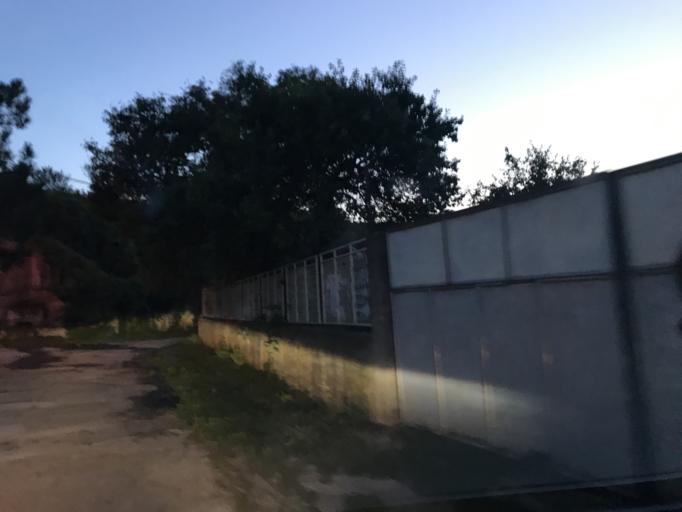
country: BG
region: Vidin
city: Bregovo
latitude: 44.1235
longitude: 22.5659
